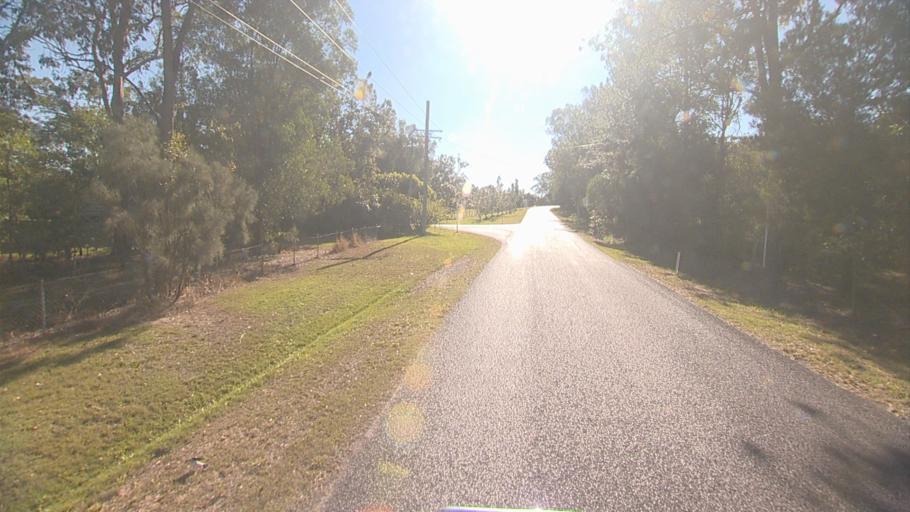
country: AU
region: Queensland
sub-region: Logan
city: Chambers Flat
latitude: -27.7406
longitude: 153.0791
